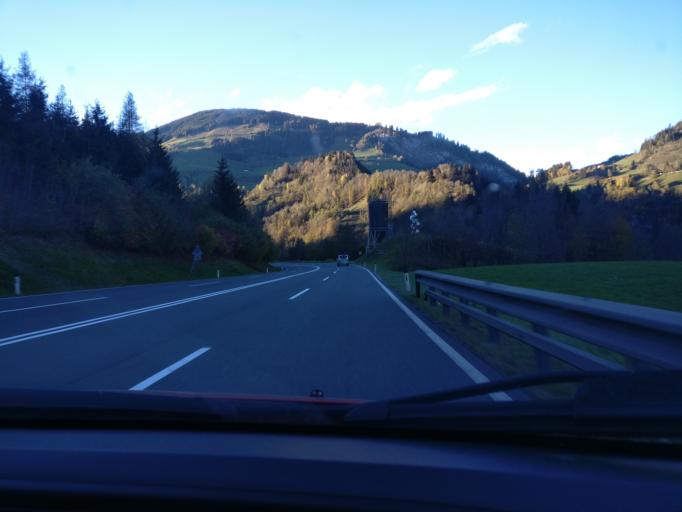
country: AT
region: Salzburg
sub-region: Politischer Bezirk Zell am See
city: Lend
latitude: 47.3035
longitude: 13.0328
